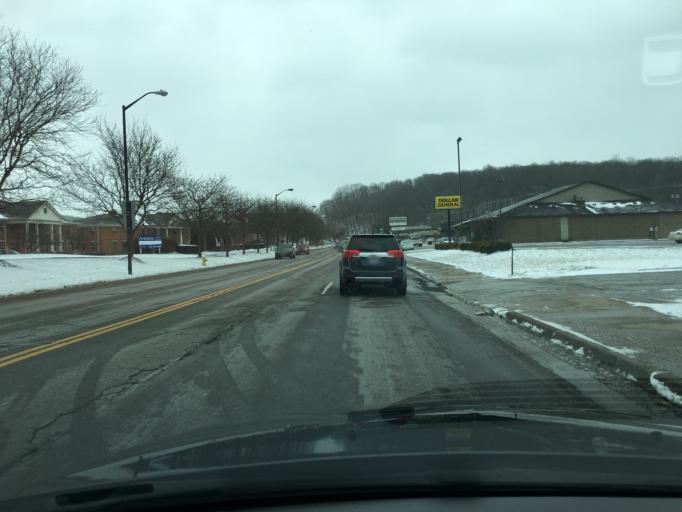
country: US
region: Ohio
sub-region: Summit County
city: Fairlawn
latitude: 41.1348
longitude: -81.5528
